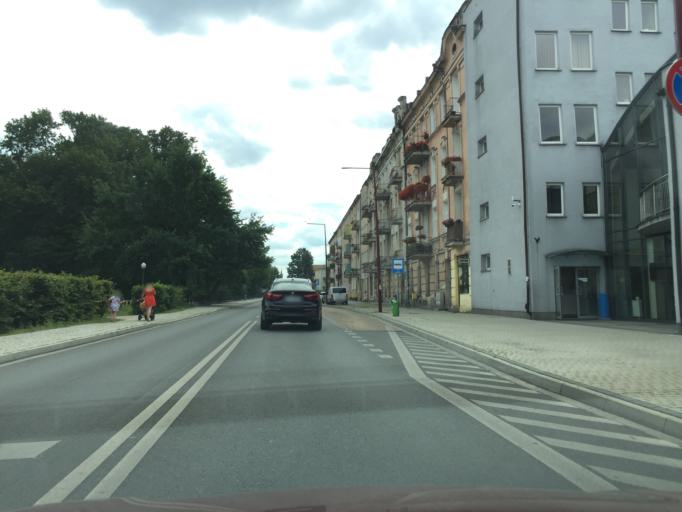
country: PL
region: Greater Poland Voivodeship
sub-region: Kalisz
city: Kalisz
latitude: 51.7584
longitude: 18.0932
